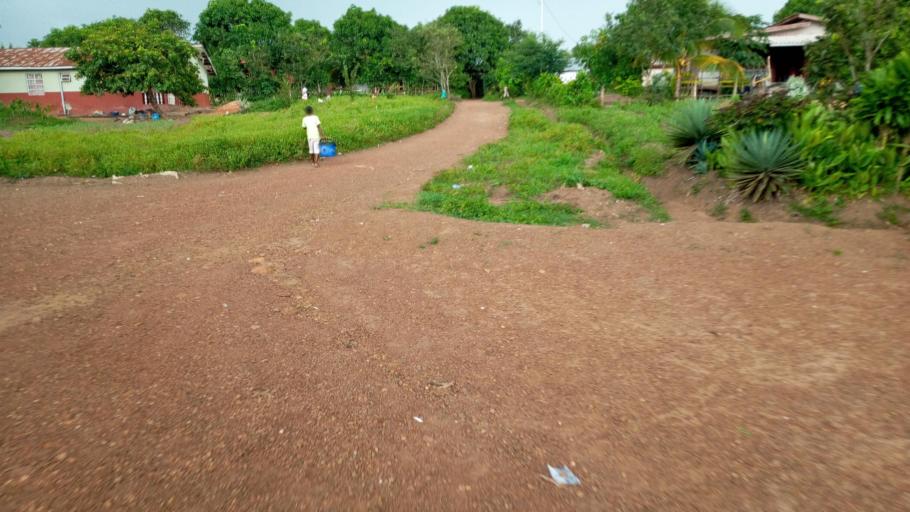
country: SL
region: Southern Province
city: Mogbwemo
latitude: 7.7802
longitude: -12.2922
